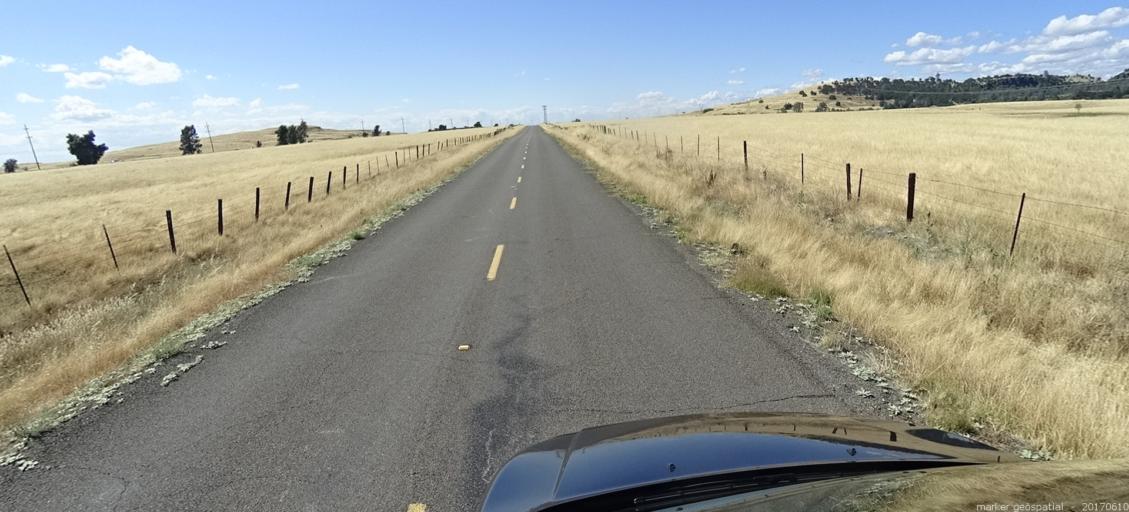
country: US
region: California
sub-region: Butte County
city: Thermalito
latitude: 39.5606
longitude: -121.6012
